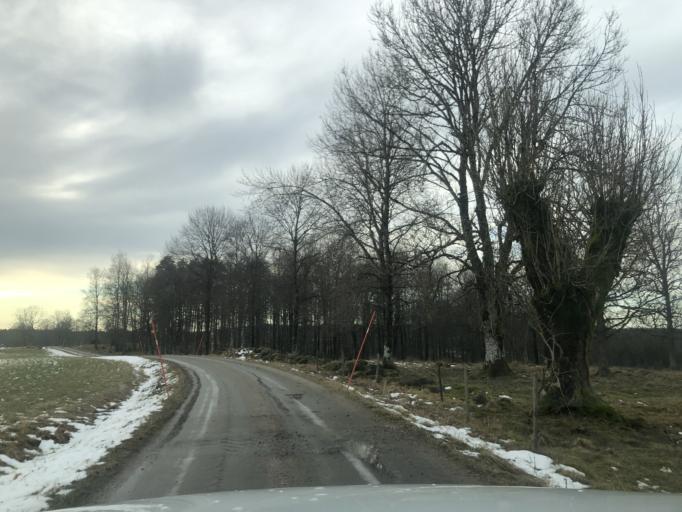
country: SE
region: Vaestra Goetaland
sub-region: Ulricehamns Kommun
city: Ulricehamn
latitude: 57.7986
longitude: 13.4914
